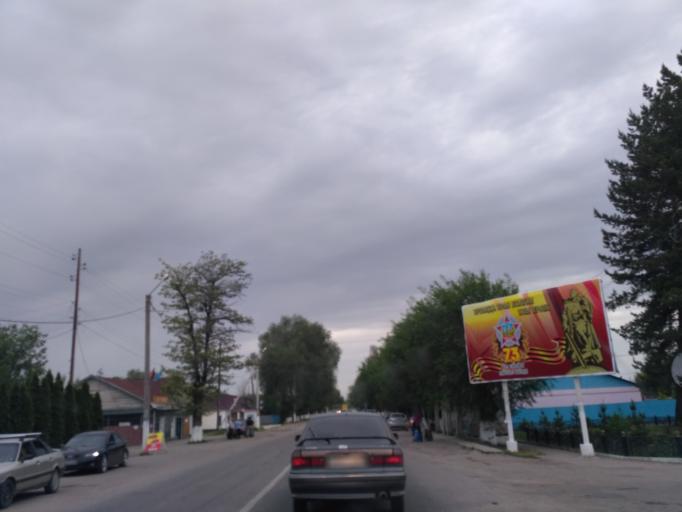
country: KZ
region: Almaty Oblysy
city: Burunday
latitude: 43.4602
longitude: 76.7258
